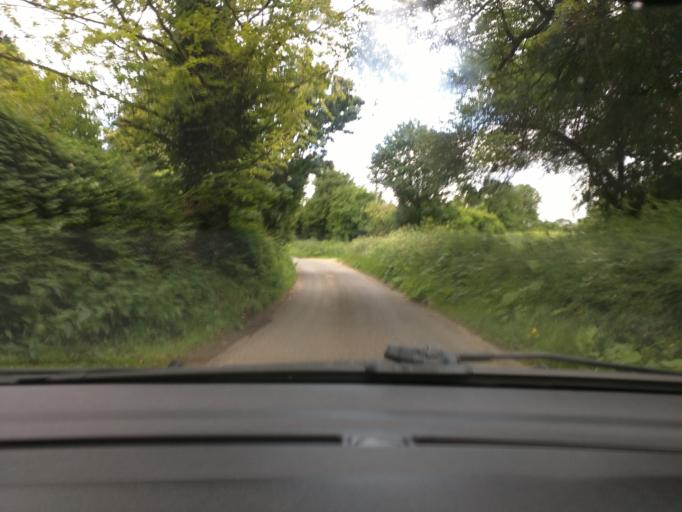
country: GB
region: England
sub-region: Suffolk
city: Saxmundham
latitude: 52.2285
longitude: 1.4721
